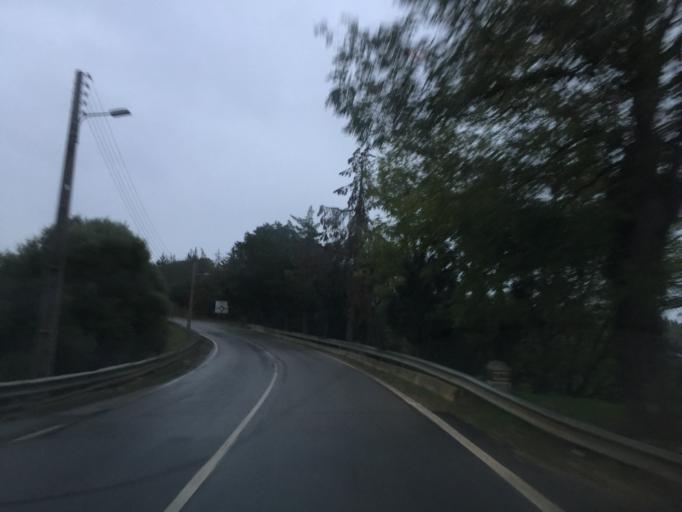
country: PT
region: Portalegre
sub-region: Avis
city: Avis
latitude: 39.0586
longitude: -7.8969
